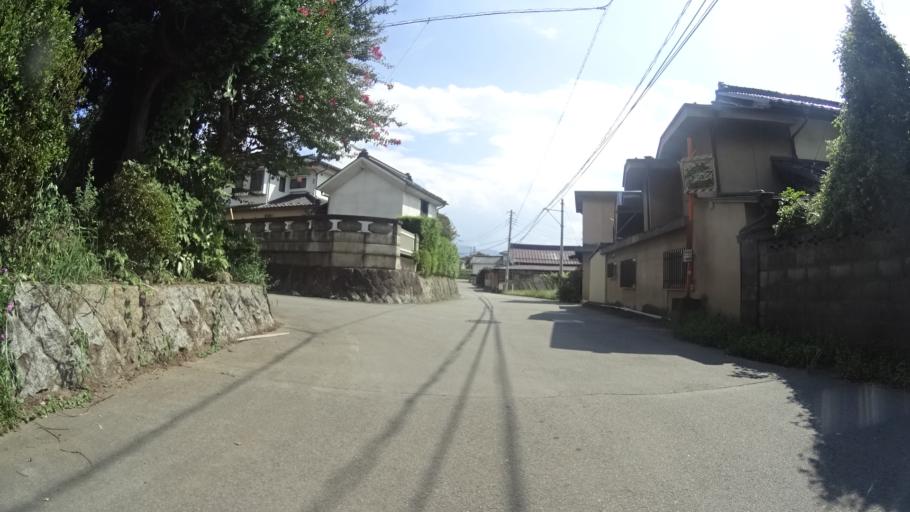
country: JP
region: Yamanashi
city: Enzan
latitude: 35.7175
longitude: 138.7337
